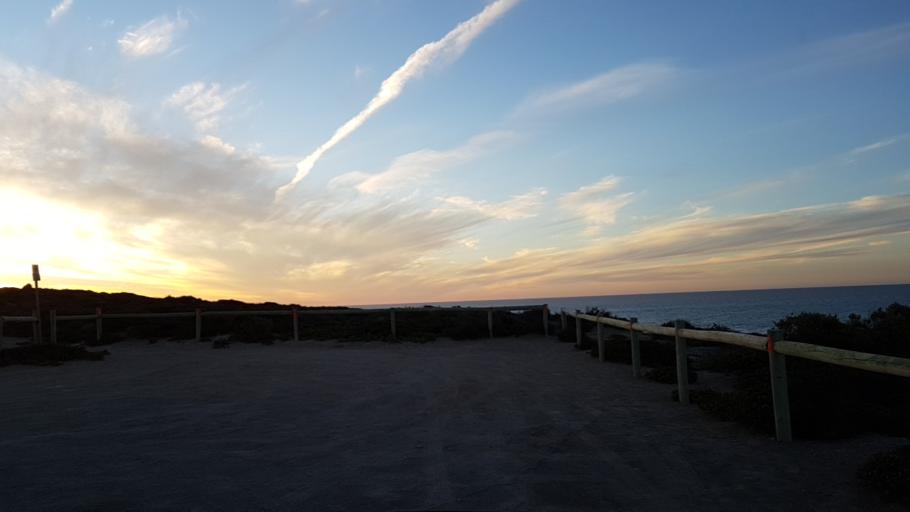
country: AU
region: South Australia
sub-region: Yorke Peninsula
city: Port Victoria
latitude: -34.8963
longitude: 137.0117
